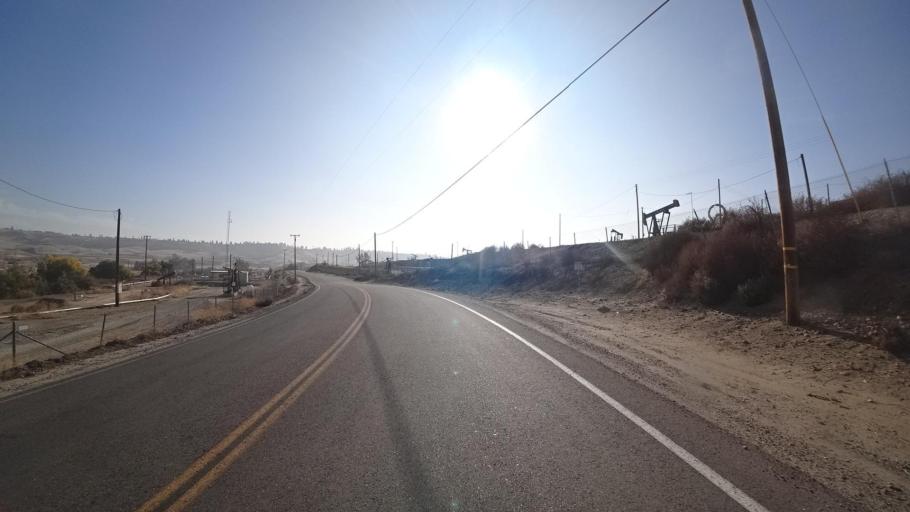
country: US
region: California
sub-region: Kern County
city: Oildale
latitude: 35.4310
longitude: -118.9547
